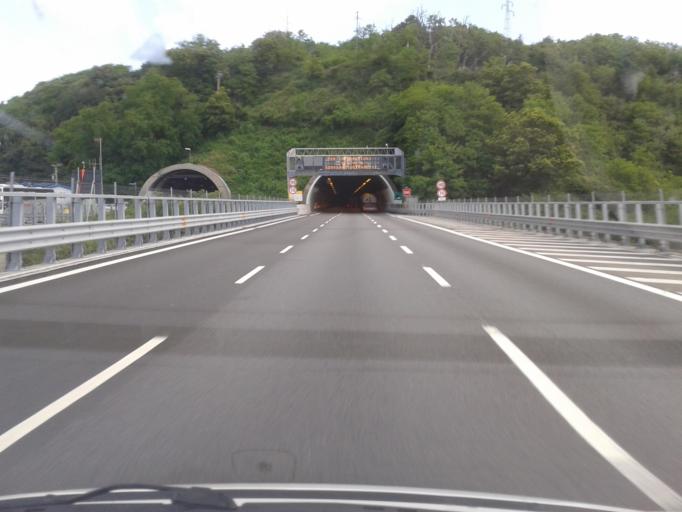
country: IT
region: Liguria
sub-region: Provincia di Genova
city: Mele
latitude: 44.4576
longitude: 8.7447
